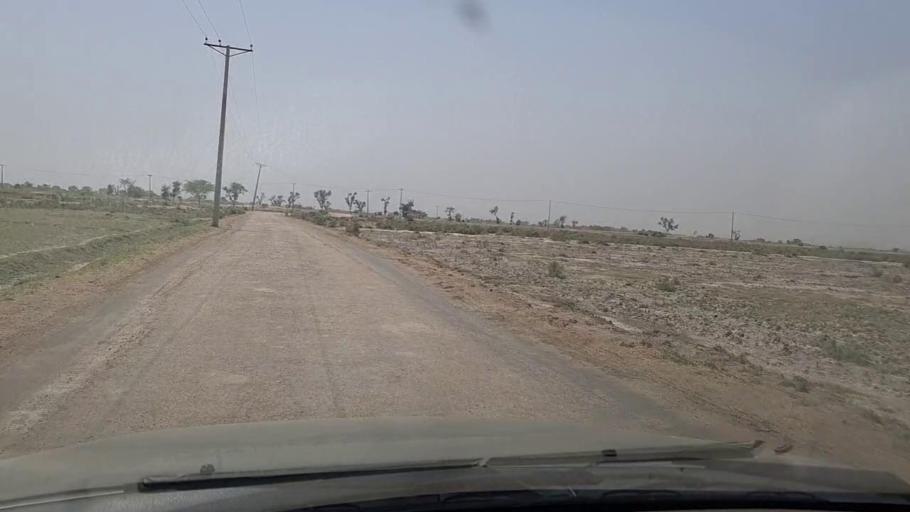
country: PK
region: Sindh
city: Miro Khan
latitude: 27.7651
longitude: 68.1360
